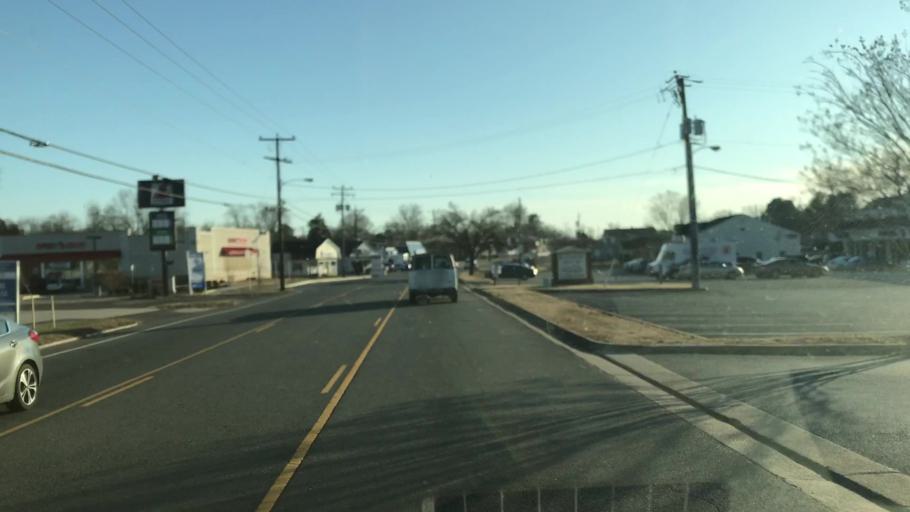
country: US
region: Virginia
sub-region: City of Fredericksburg
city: Fredericksburg
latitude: 38.2774
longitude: -77.4811
